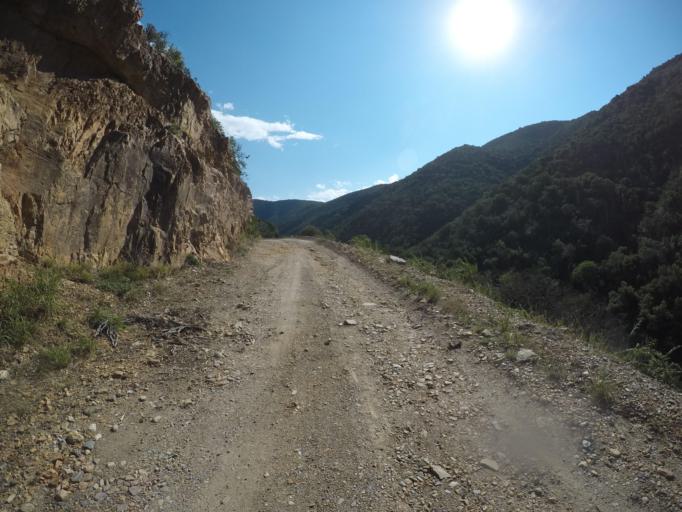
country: ZA
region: Eastern Cape
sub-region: Cacadu District Municipality
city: Kareedouw
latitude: -33.6553
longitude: 24.3586
